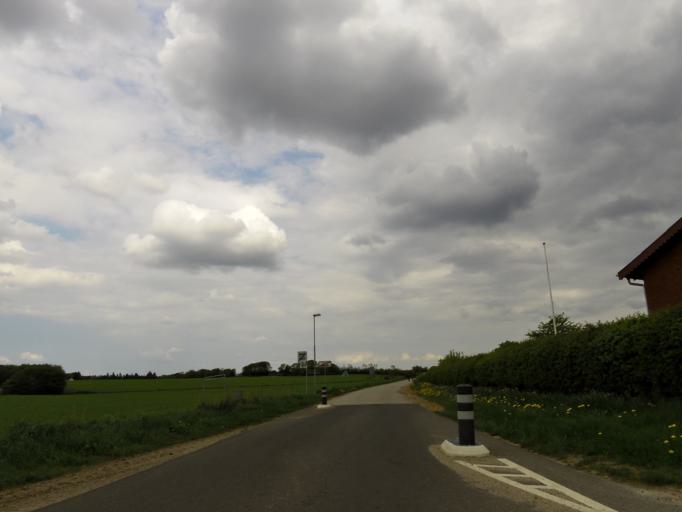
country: DK
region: Central Jutland
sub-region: Holstebro Kommune
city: Vinderup
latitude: 56.5244
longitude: 8.7874
